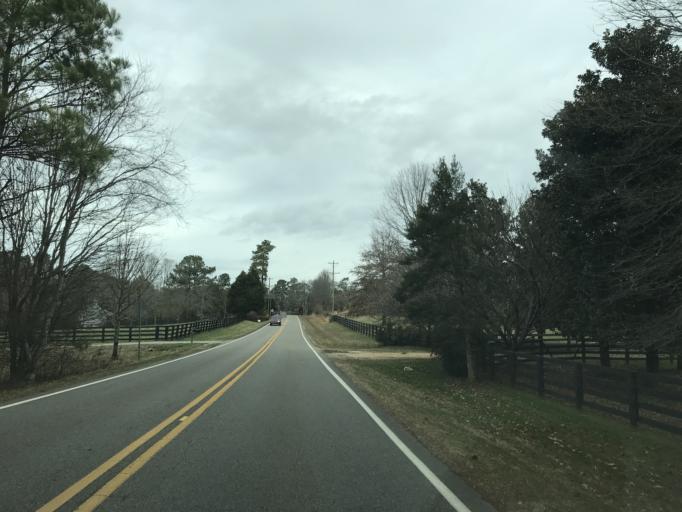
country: US
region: Georgia
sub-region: Fulton County
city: Milton
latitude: 34.1905
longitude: -84.3416
